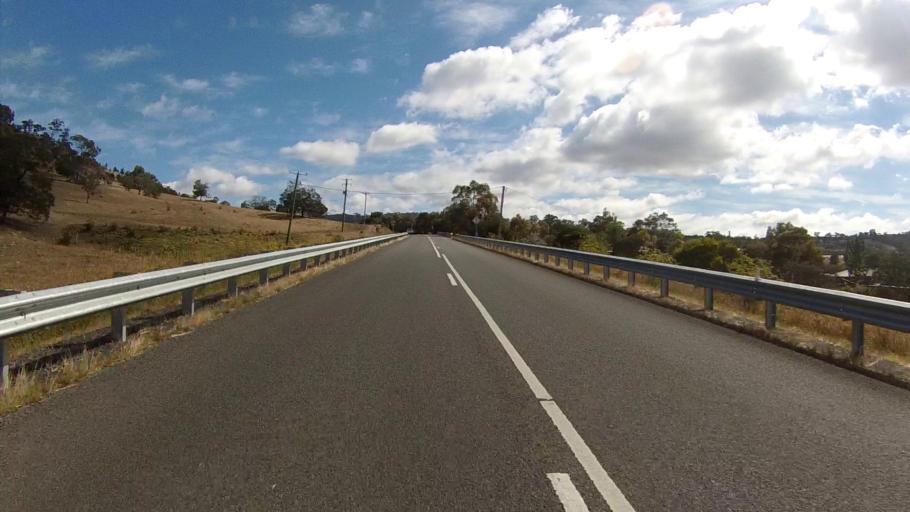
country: AU
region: Tasmania
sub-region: Brighton
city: Old Beach
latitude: -42.7357
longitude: 147.2888
